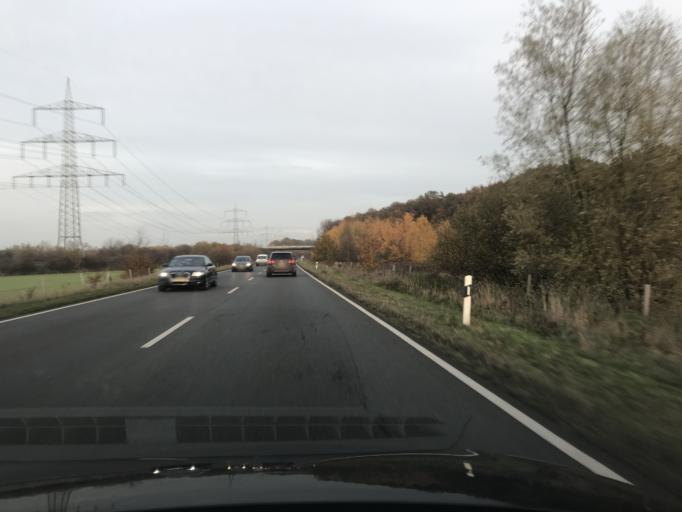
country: DE
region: North Rhine-Westphalia
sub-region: Regierungsbezirk Arnsberg
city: Hamm
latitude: 51.7232
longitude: 7.7728
